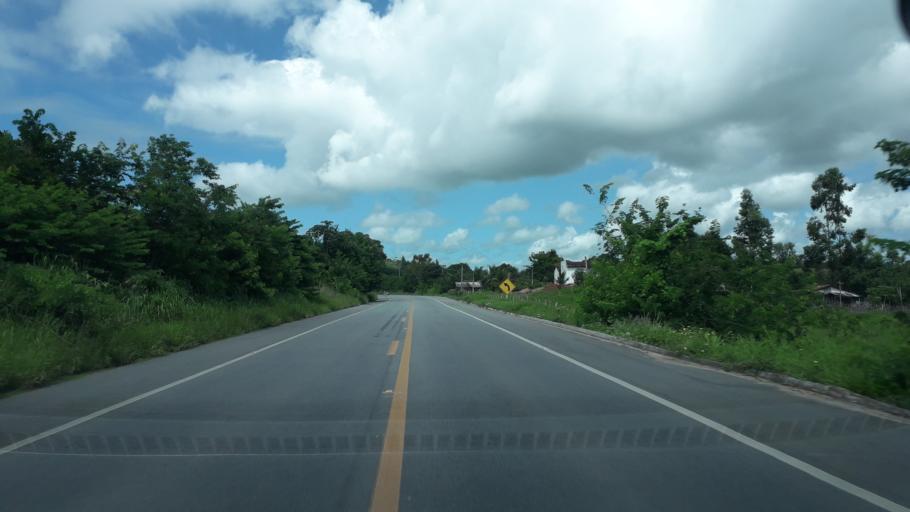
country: BR
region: Alagoas
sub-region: Uniao Dos Palmares
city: Uniao dos Palmares
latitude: -9.2169
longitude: -36.0322
